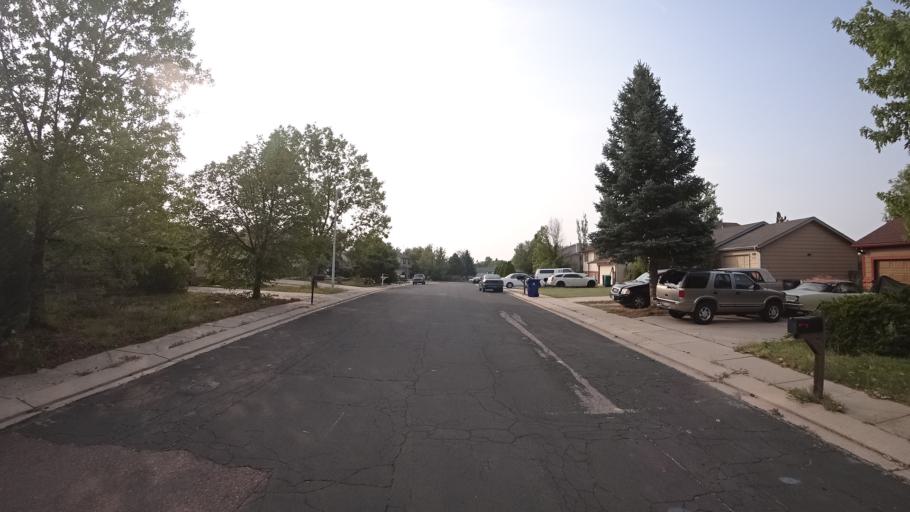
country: US
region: Colorado
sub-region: El Paso County
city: Stratmoor
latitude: 38.8016
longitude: -104.7483
